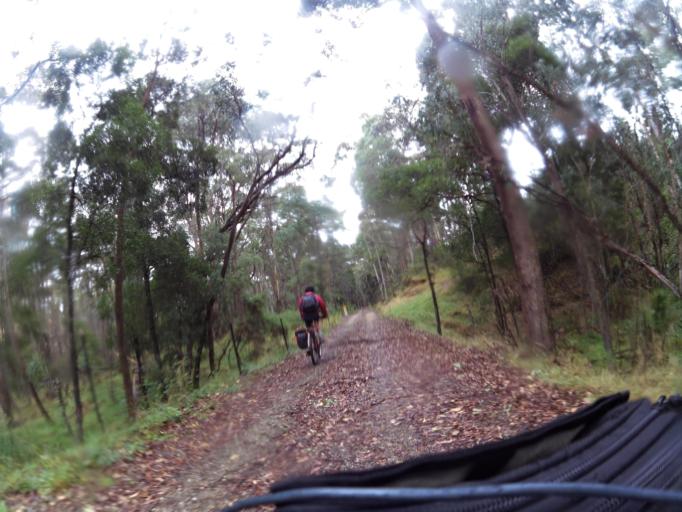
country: AU
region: New South Wales
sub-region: Greater Hume Shire
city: Holbrook
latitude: -36.1830
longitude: 147.5014
